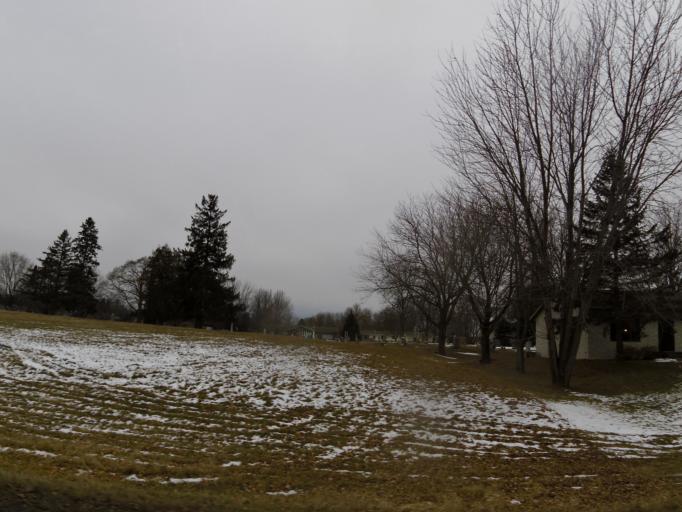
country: US
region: Minnesota
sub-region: Carver County
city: Watertown
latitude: 44.9595
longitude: -93.8410
